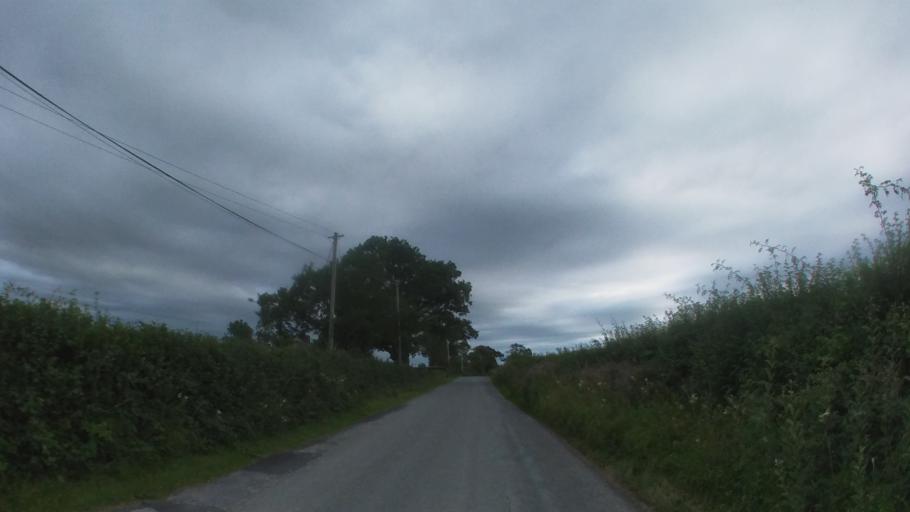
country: IE
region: Leinster
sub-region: Kilkenny
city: Kilkenny
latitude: 52.6928
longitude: -7.2153
